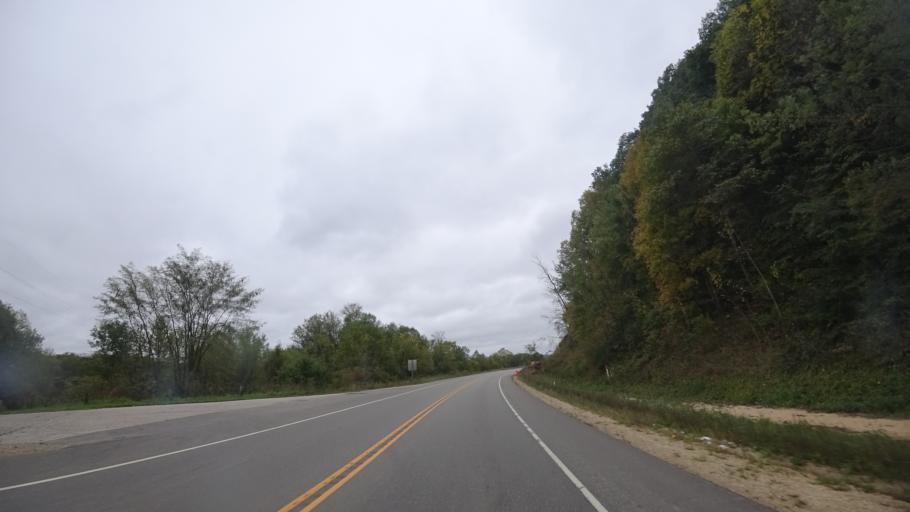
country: US
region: Wisconsin
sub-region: Grant County
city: Boscobel
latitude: 43.1662
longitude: -90.7054
